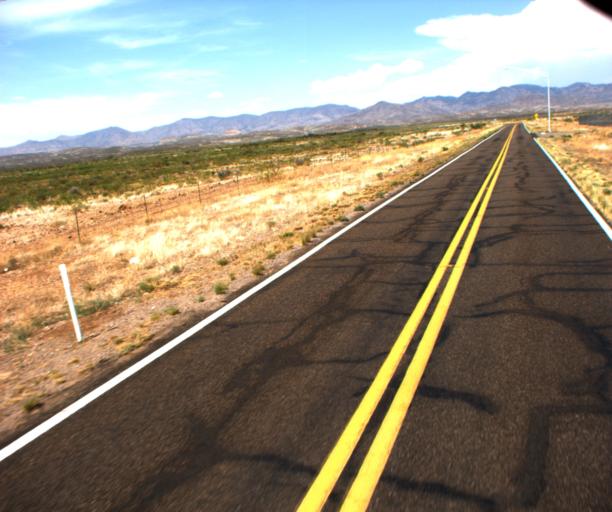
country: US
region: Arizona
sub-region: Greenlee County
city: Clifton
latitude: 32.9606
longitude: -109.2105
